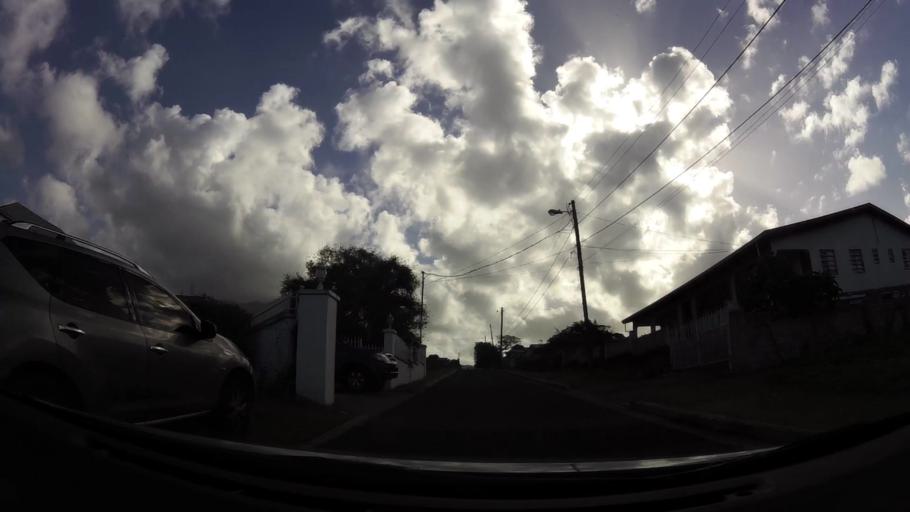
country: KN
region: Saint Paul Charlestown
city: Charlestown
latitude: 17.1387
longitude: -62.6245
